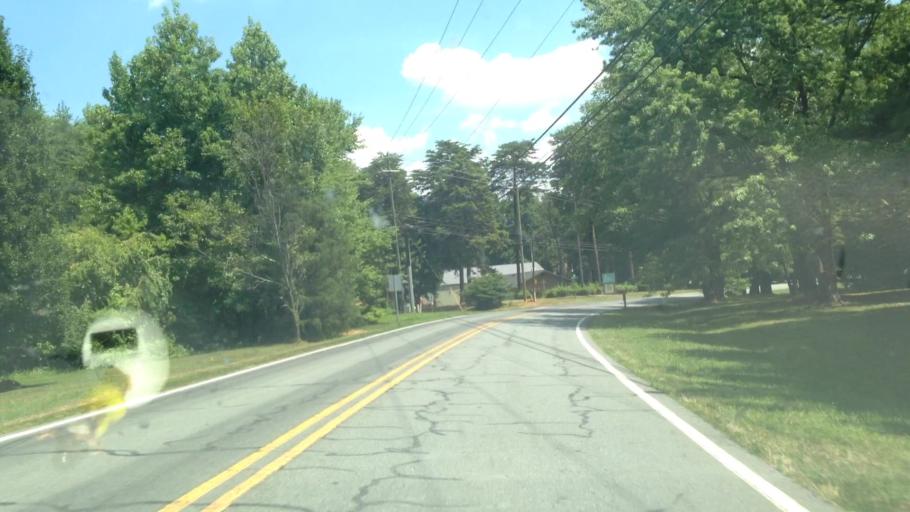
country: US
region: North Carolina
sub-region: Forsyth County
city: Kernersville
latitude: 36.1533
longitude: -80.0610
